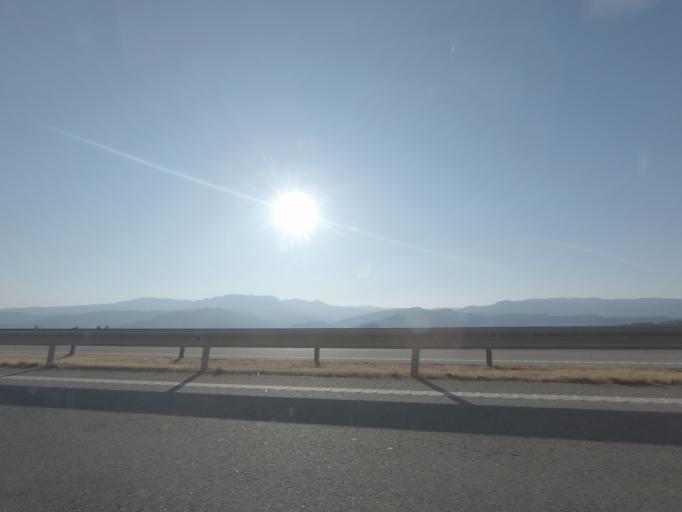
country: PT
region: Vila Real
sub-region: Vila Real
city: Vila Real
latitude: 41.2326
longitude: -7.7318
